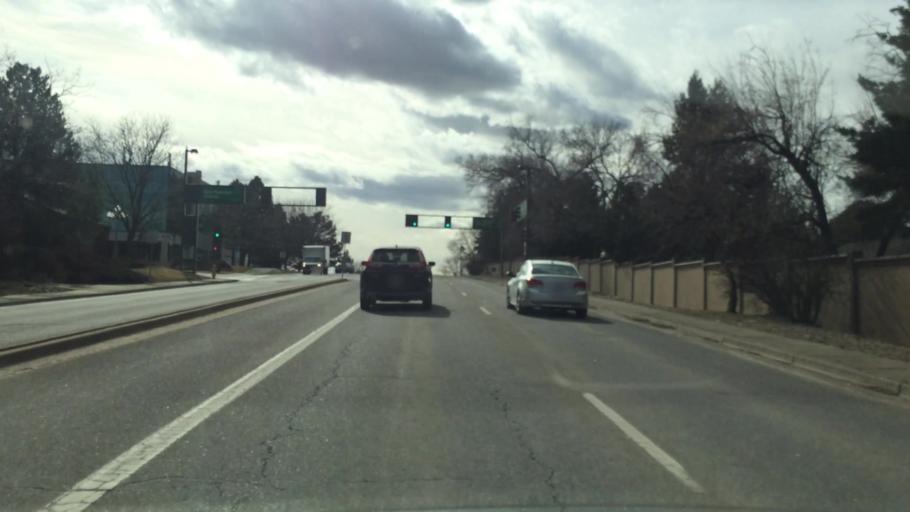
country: US
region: Colorado
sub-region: Arapahoe County
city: Castlewood
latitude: 39.5994
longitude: -104.9042
